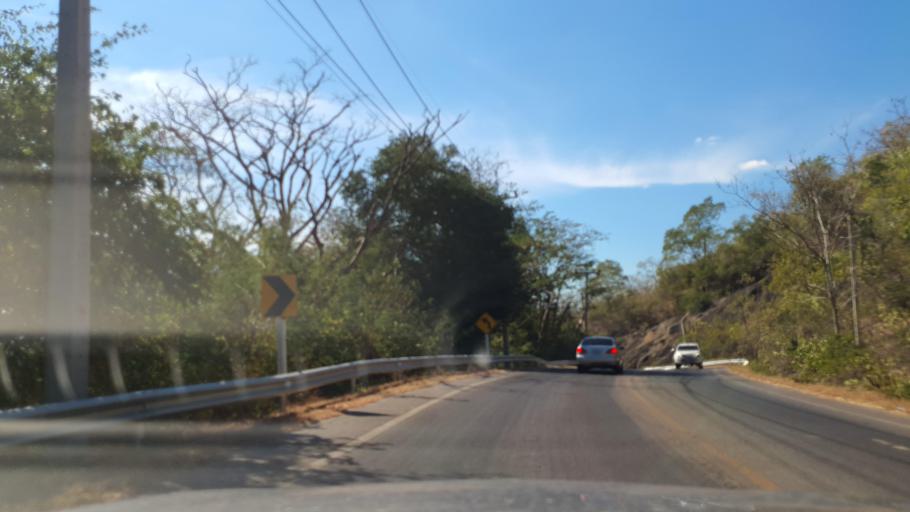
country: TH
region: Kalasin
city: Khao Wong
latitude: 16.7545
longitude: 104.1230
